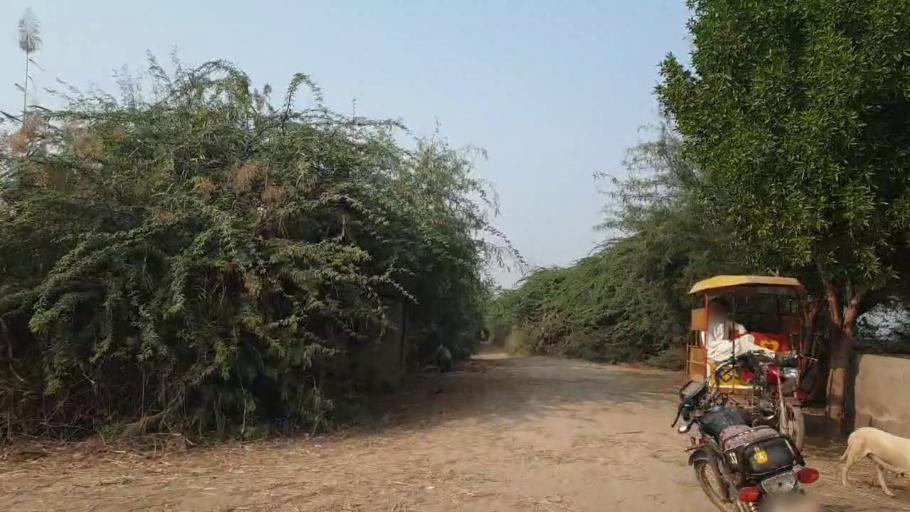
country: PK
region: Sindh
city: Tando Muhammad Khan
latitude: 25.1433
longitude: 68.6168
